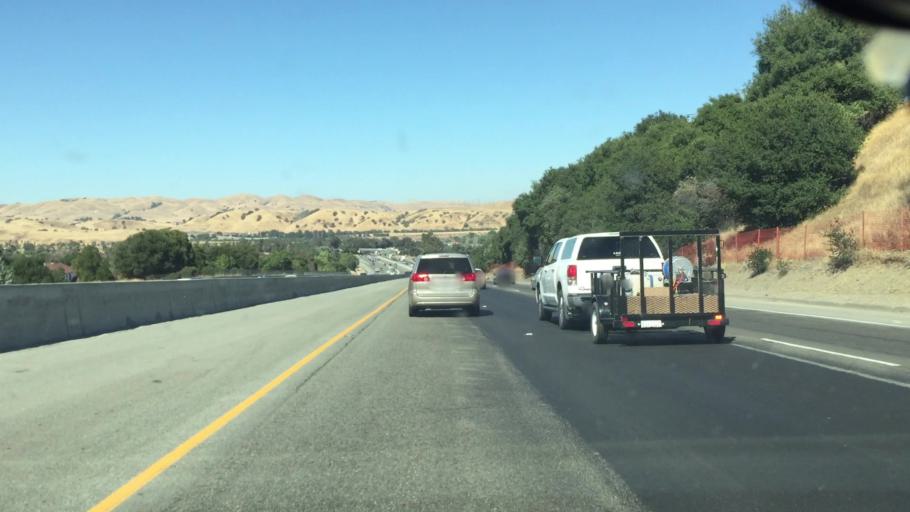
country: US
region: California
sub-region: Alameda County
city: Fremont
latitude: 37.5683
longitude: -121.8947
